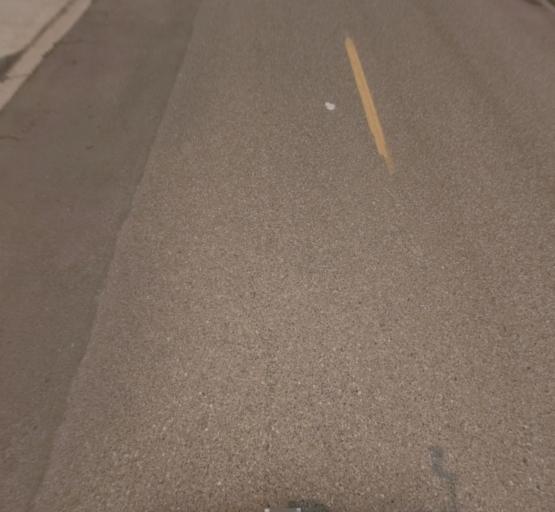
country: US
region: California
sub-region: Madera County
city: Madera Acres
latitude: 37.0258
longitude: -120.0615
